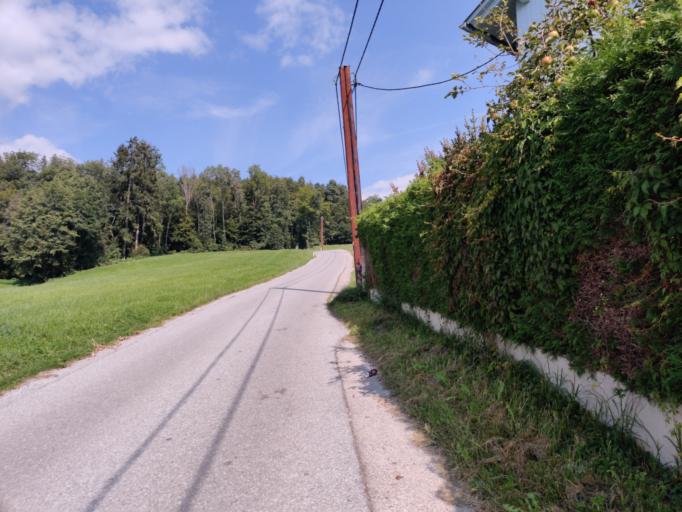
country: AT
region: Styria
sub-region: Politischer Bezirk Graz-Umgebung
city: Kumberg
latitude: 47.1294
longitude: 15.5272
